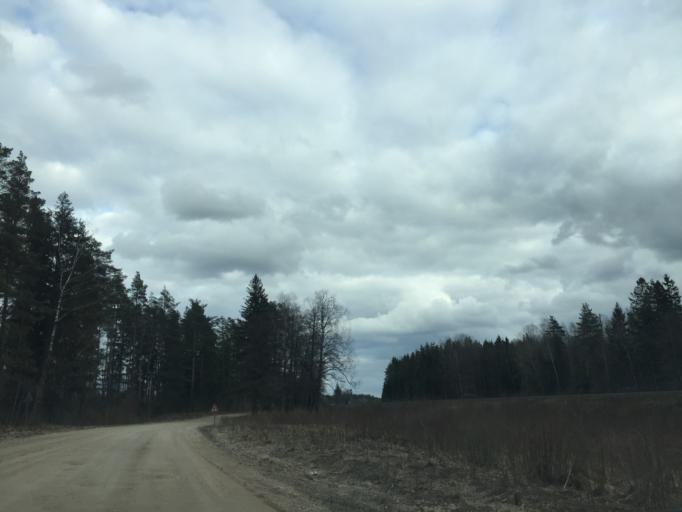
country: LV
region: Ogre
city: Jumprava
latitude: 56.5633
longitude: 24.9151
